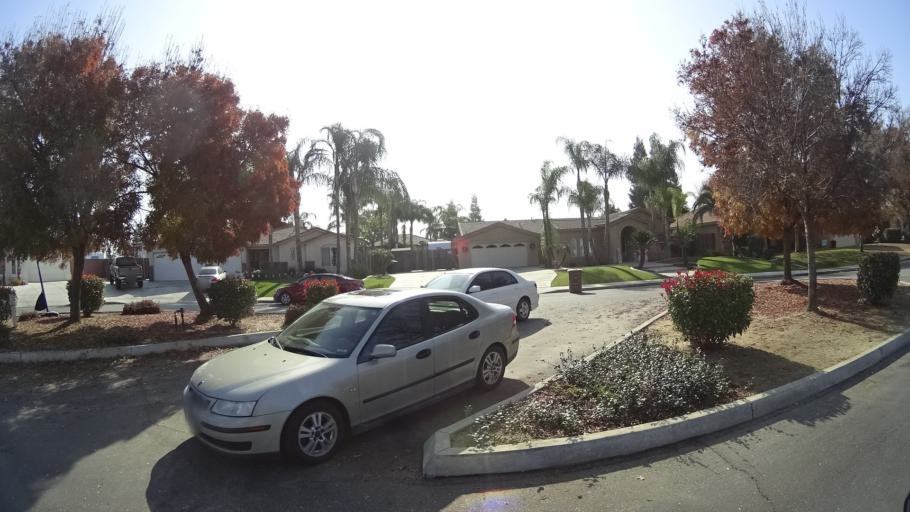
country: US
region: California
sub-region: Kern County
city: Greenacres
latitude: 35.4239
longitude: -119.1109
